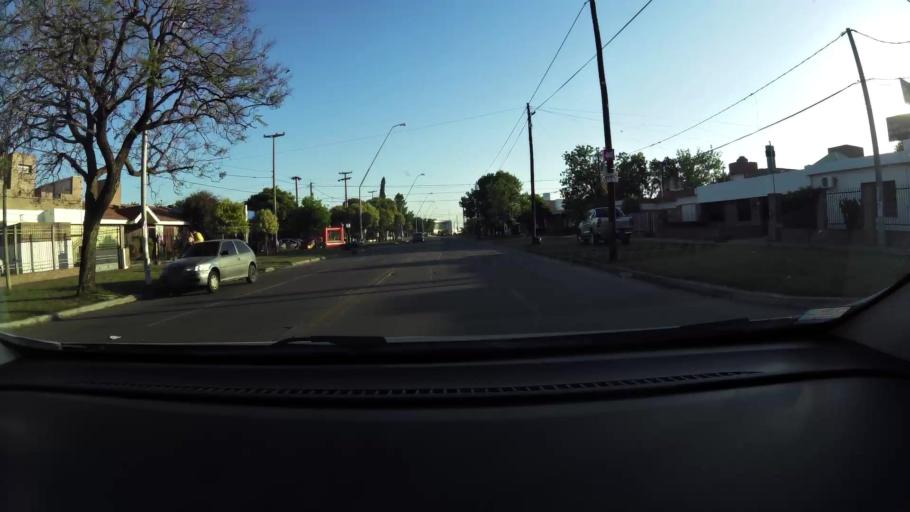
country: AR
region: Cordoba
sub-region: Departamento de Capital
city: Cordoba
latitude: -31.3778
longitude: -64.2146
